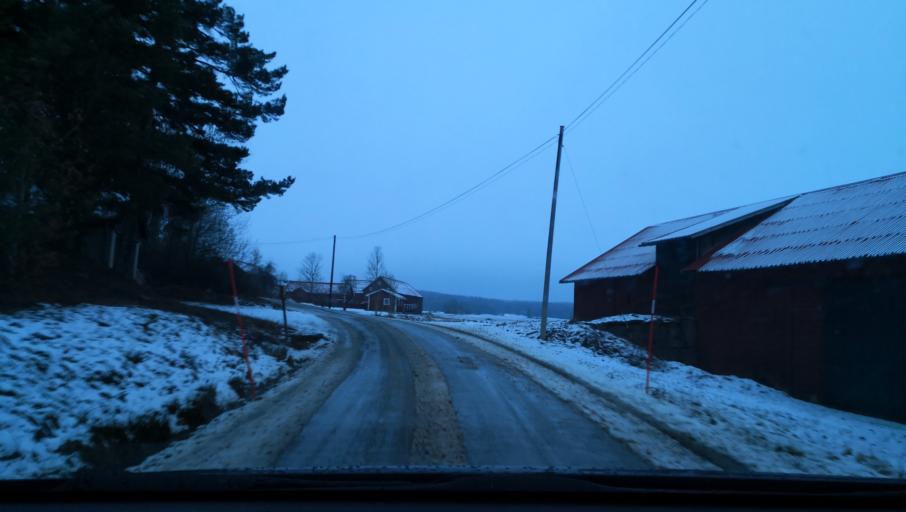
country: SE
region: Vaestmanland
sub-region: Kungsors Kommun
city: Kungsoer
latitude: 59.3950
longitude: 16.2095
